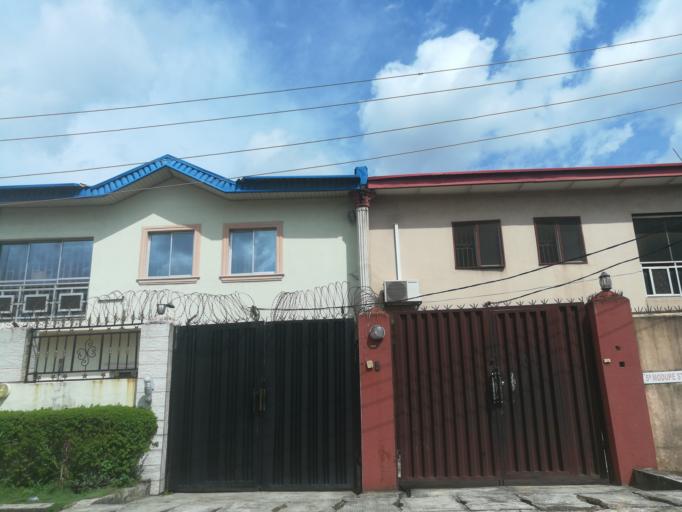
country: NG
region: Lagos
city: Somolu
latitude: 6.5291
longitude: 3.3834
